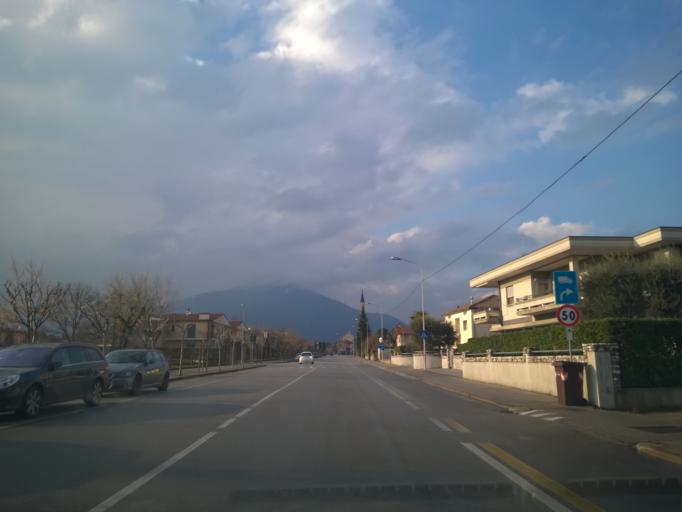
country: IT
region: Veneto
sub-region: Provincia di Vicenza
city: Zane
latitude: 45.7167
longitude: 11.4641
